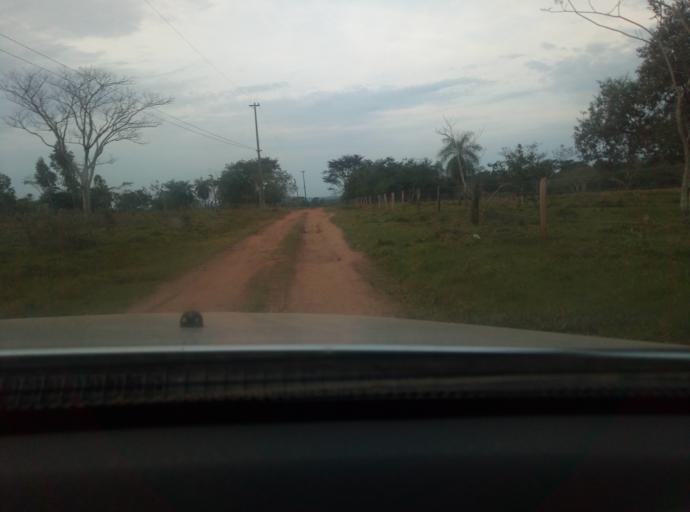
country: PY
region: Caaguazu
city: Carayao
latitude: -25.1483
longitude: -56.3843
